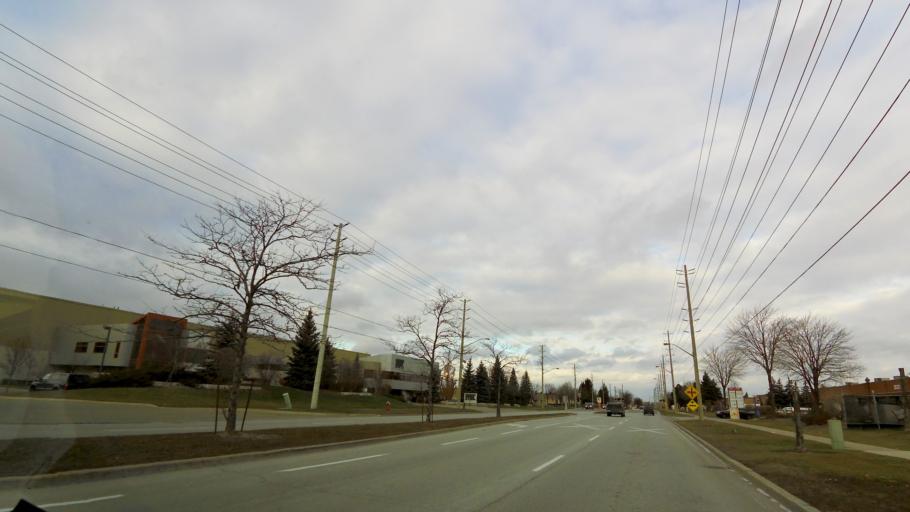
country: CA
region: Ontario
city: Brampton
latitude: 43.7569
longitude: -79.7045
